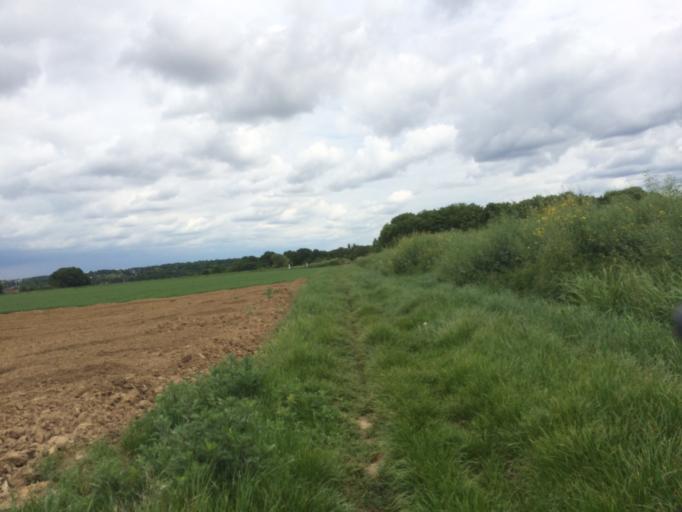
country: FR
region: Ile-de-France
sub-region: Departement de l'Essonne
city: Ballainvilliers
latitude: 48.6688
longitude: 2.3022
